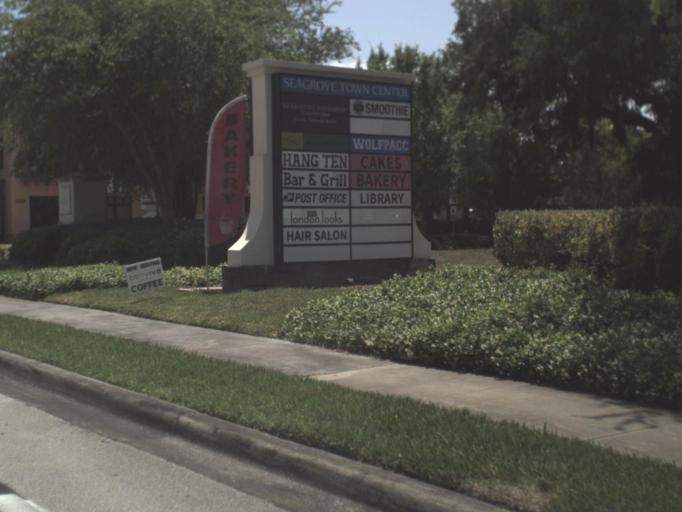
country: US
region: Florida
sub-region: Saint Johns County
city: Saint Augustine Beach
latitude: 29.8450
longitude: -81.2771
